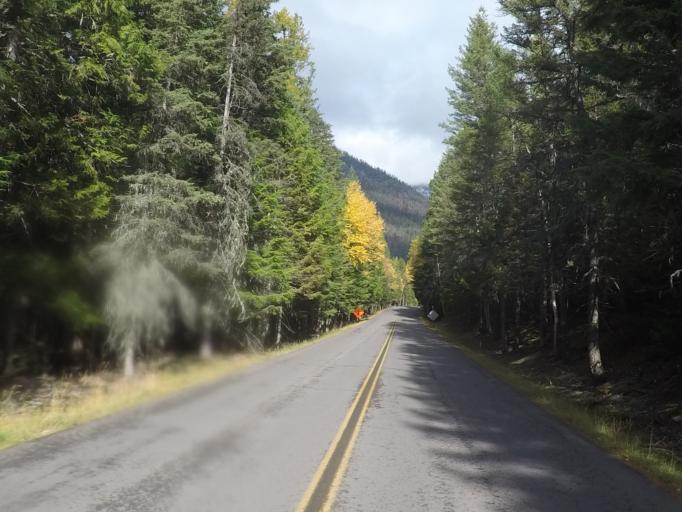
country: US
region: Montana
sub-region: Flathead County
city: Columbia Falls
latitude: 48.6350
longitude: -113.8634
